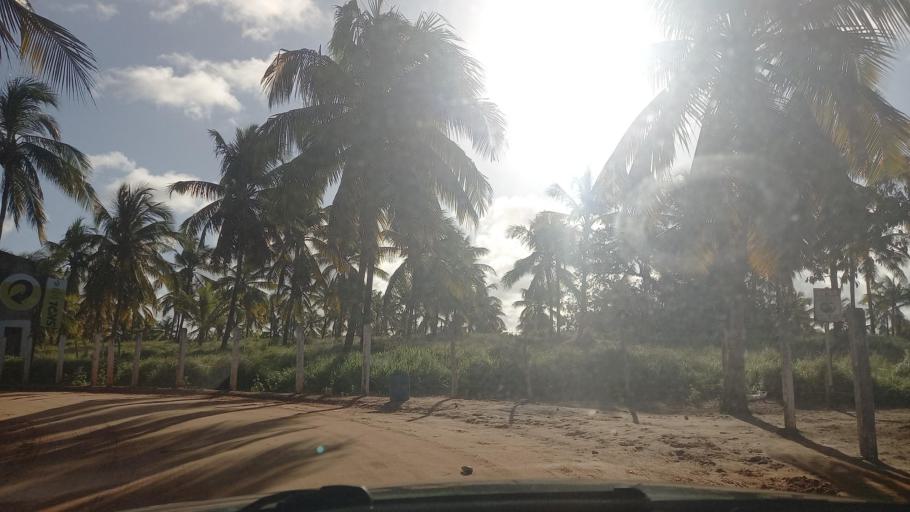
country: BR
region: Alagoas
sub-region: Marechal Deodoro
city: Marechal Deodoro
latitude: -9.8603
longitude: -35.9097
